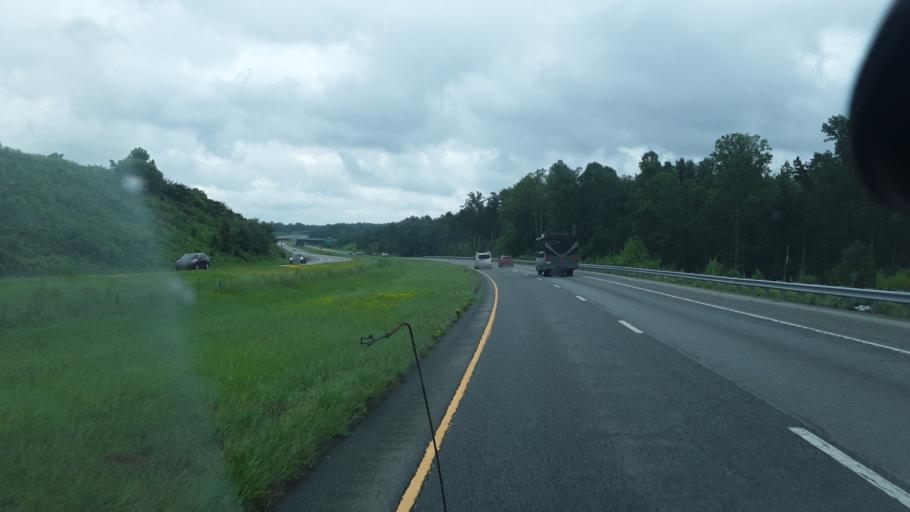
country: US
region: North Carolina
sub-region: Randolph County
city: Archdale
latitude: 35.9359
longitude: -79.9563
